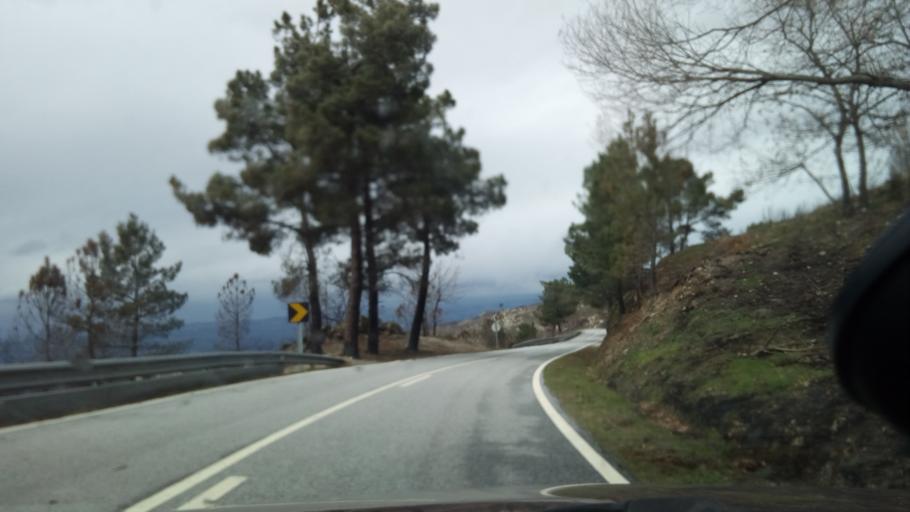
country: PT
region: Guarda
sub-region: Manteigas
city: Manteigas
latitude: 40.4589
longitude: -7.5878
